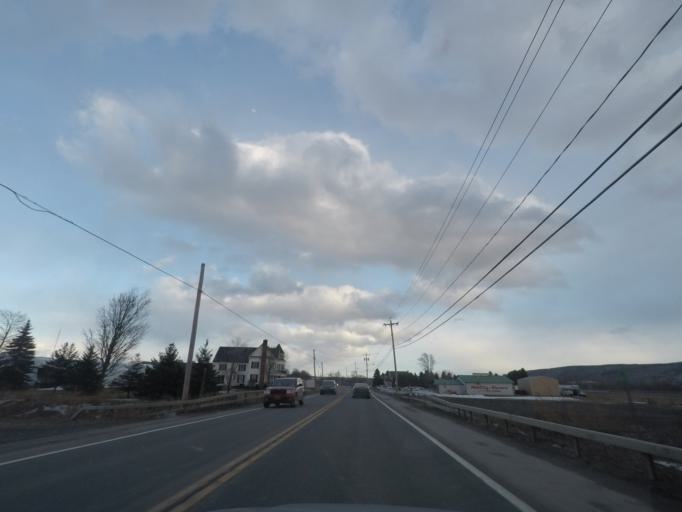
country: US
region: New York
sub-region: Oneida County
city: Utica
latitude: 43.0967
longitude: -75.1478
